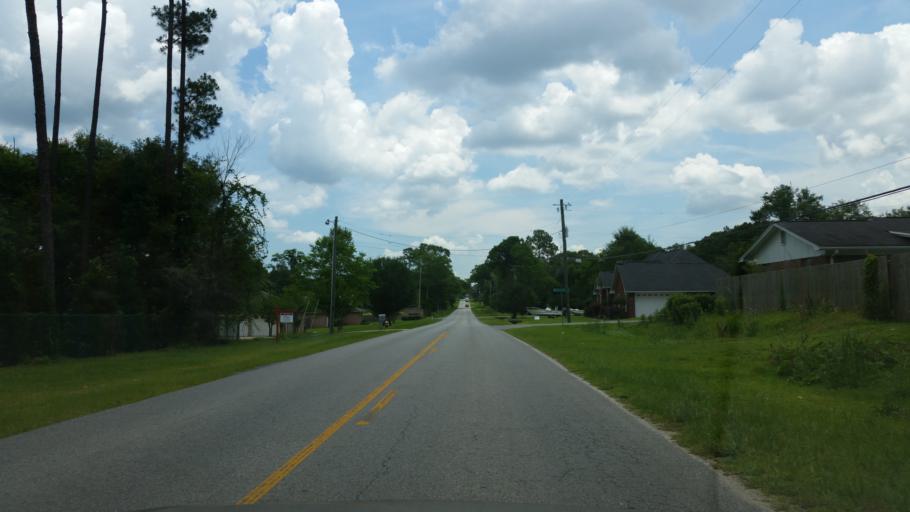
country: US
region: Florida
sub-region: Escambia County
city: Gonzalez
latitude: 30.5483
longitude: -87.2913
